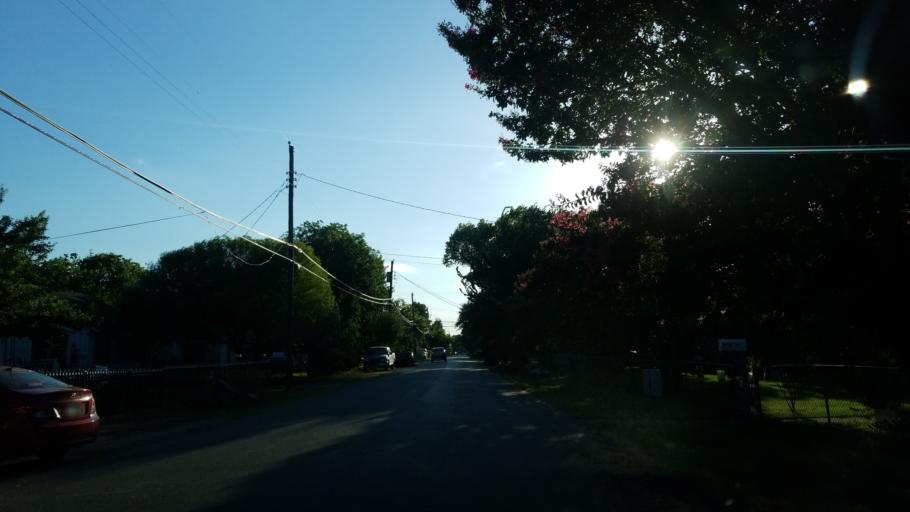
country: US
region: Texas
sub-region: Dallas County
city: Balch Springs
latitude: 32.7757
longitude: -96.6954
